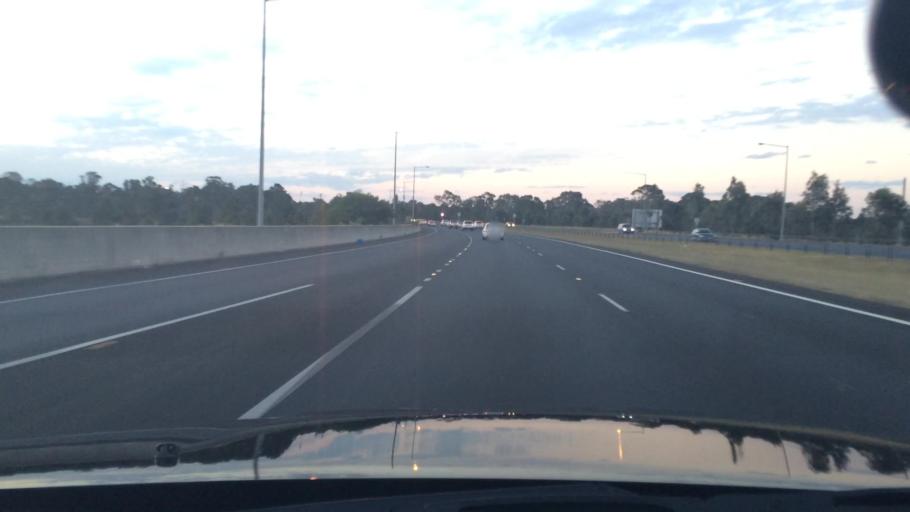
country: AU
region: New South Wales
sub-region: Blacktown
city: Doonside
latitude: -33.7852
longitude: 150.8577
